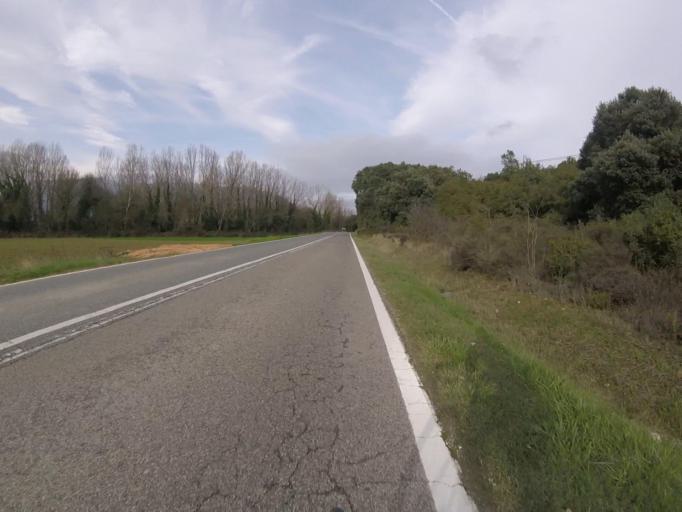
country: ES
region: Navarre
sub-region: Provincia de Navarra
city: Estella
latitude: 42.7052
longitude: -2.0677
